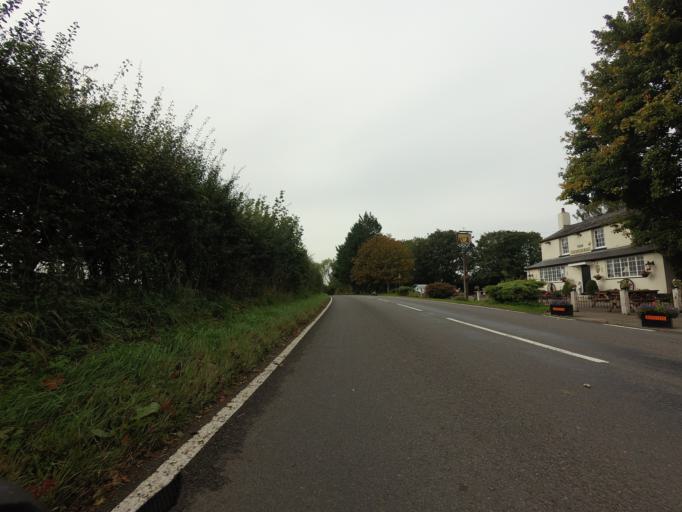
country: GB
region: England
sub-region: Hertfordshire
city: Reed
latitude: 52.0247
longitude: 0.0330
